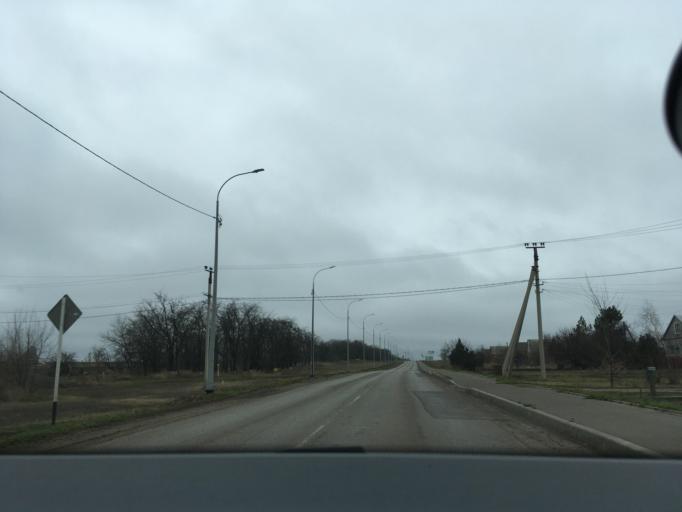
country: RU
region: Krasnodarskiy
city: Kushchevskaya
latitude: 46.5802
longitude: 39.6384
